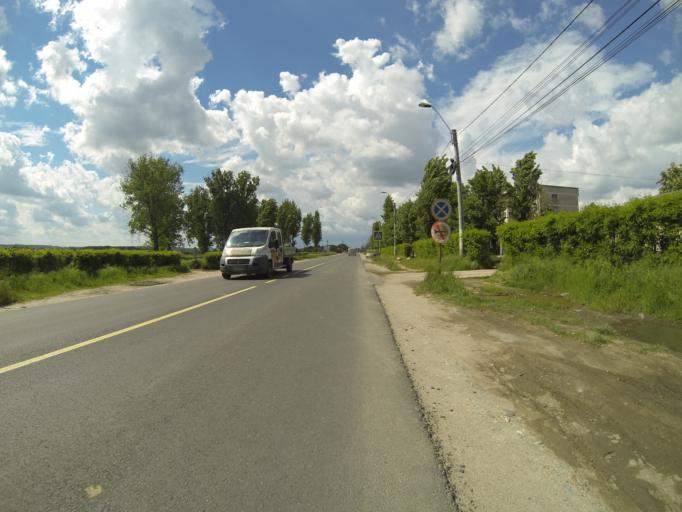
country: RO
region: Dolj
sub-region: Municipiul Craiova
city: Facai
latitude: 44.2798
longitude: 23.8079
